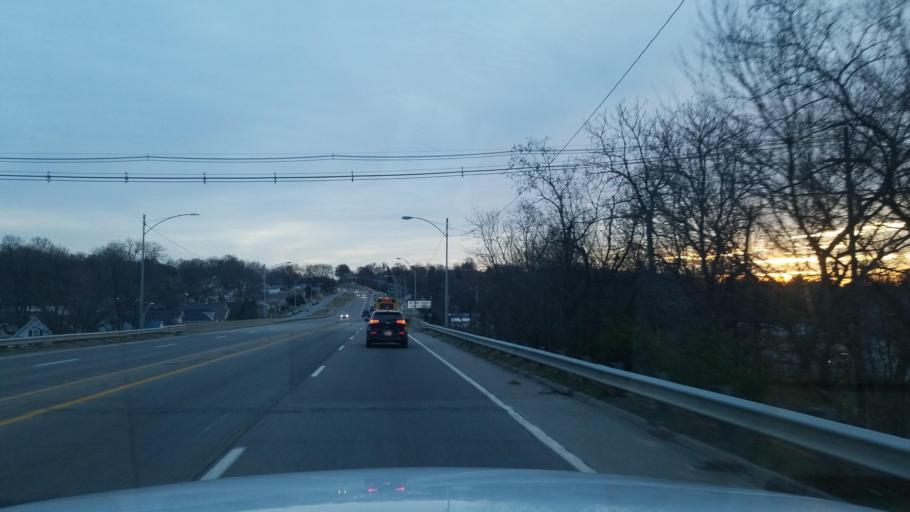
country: US
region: Indiana
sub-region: Vanderburgh County
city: Evansville
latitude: 37.9775
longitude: -87.6199
